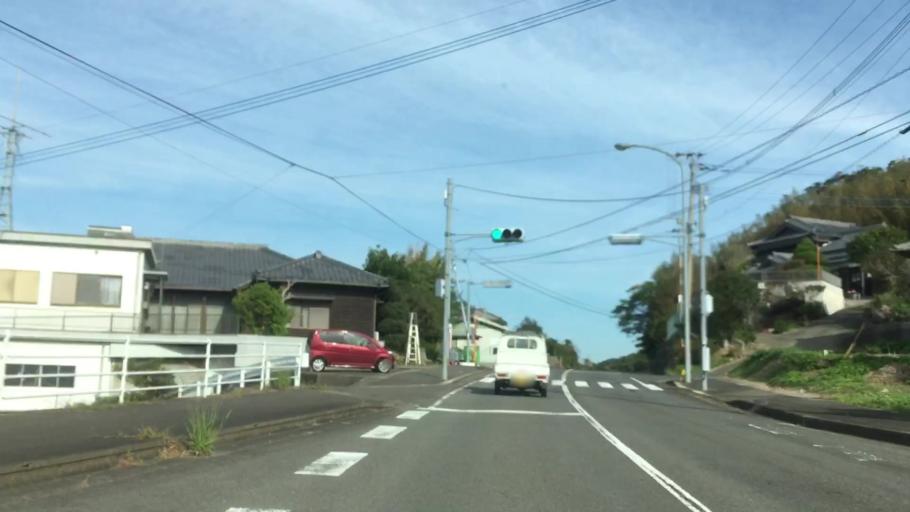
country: JP
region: Nagasaki
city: Sasebo
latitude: 33.0151
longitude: 129.6546
